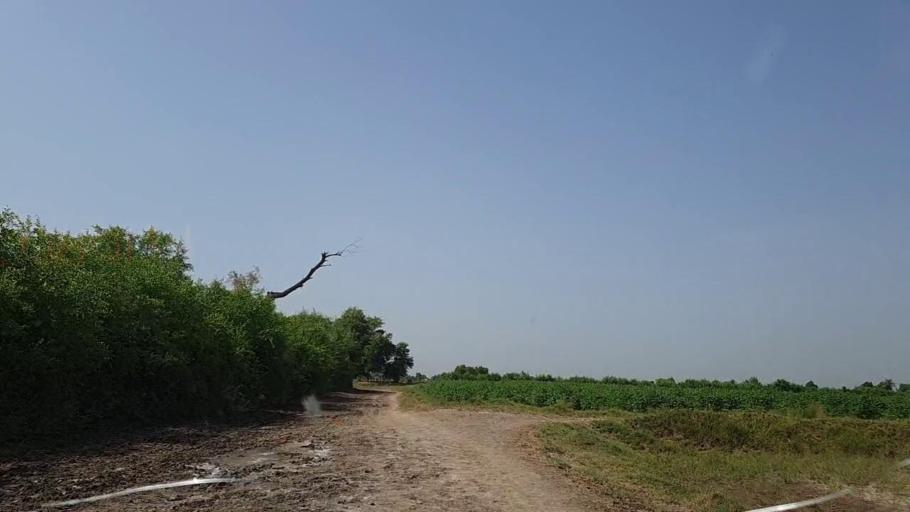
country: PK
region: Sindh
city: Naushahro Firoz
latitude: 26.8700
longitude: 68.0308
